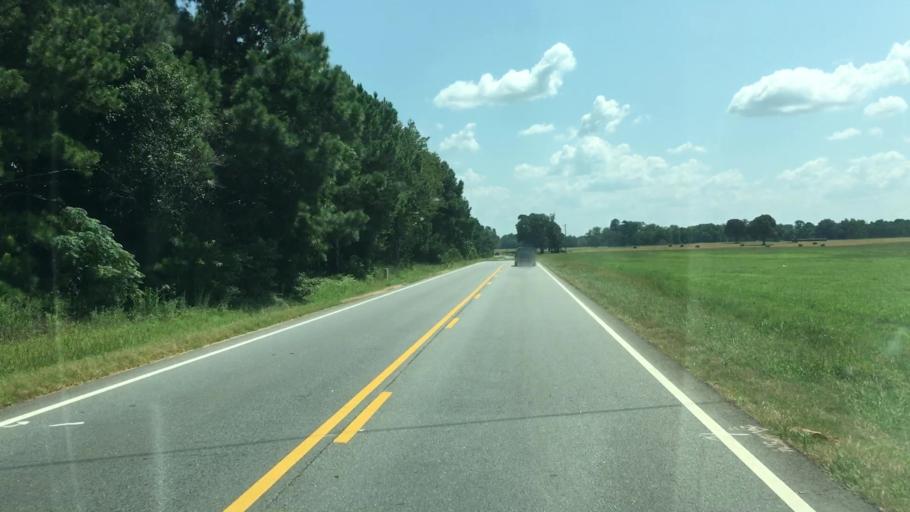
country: US
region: Georgia
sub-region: Oconee County
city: Watkinsville
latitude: 33.8049
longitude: -83.4272
